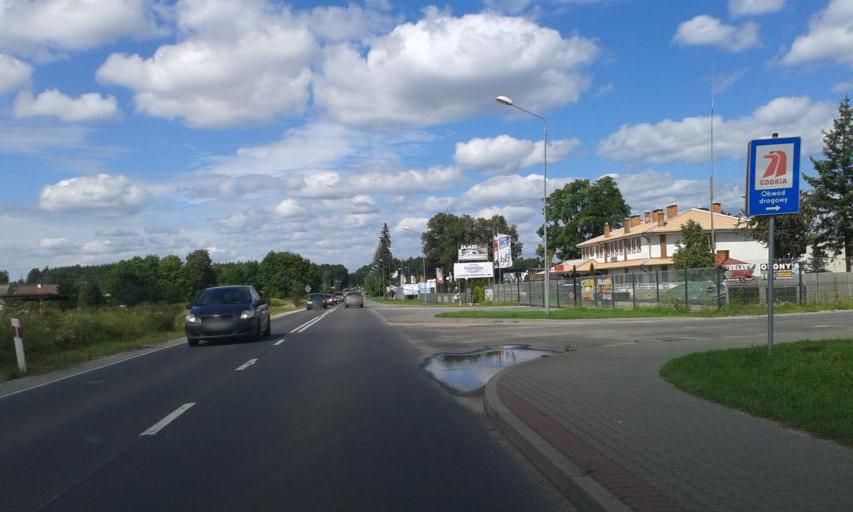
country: PL
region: West Pomeranian Voivodeship
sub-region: Powiat walecki
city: Walcz
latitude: 53.2950
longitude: 16.4571
